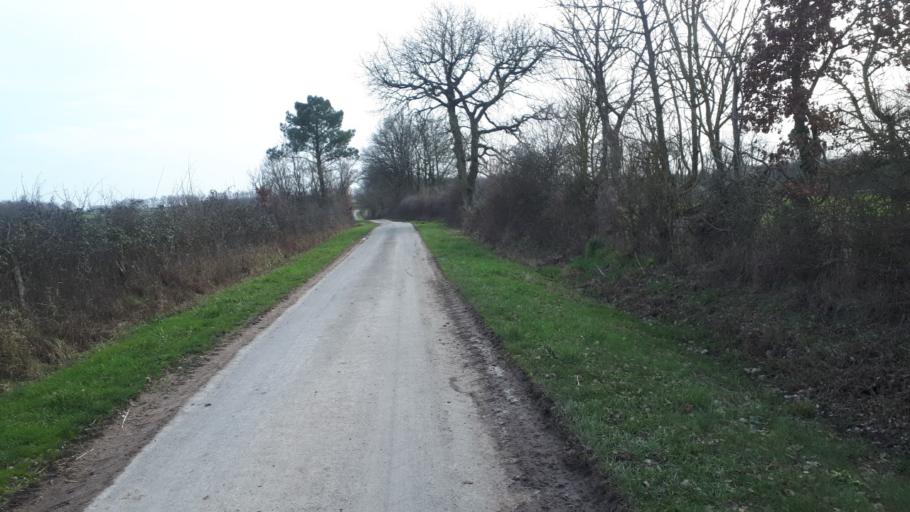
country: FR
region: Poitou-Charentes
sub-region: Departement de la Vienne
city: Archigny
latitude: 46.6259
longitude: 0.7456
